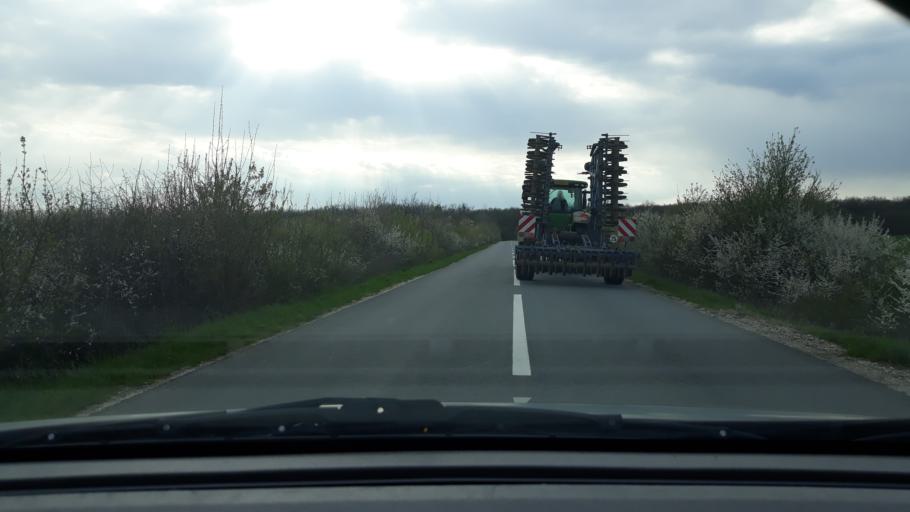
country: RO
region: Bihor
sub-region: Comuna Sacueni
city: Cubulcut
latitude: 47.3581
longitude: 22.2130
